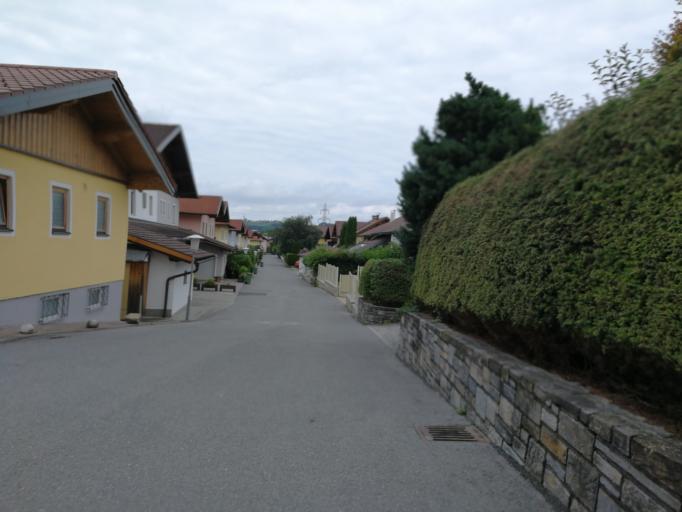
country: DE
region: Bavaria
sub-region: Upper Bavaria
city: Ainring
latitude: 47.7912
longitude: 12.9620
